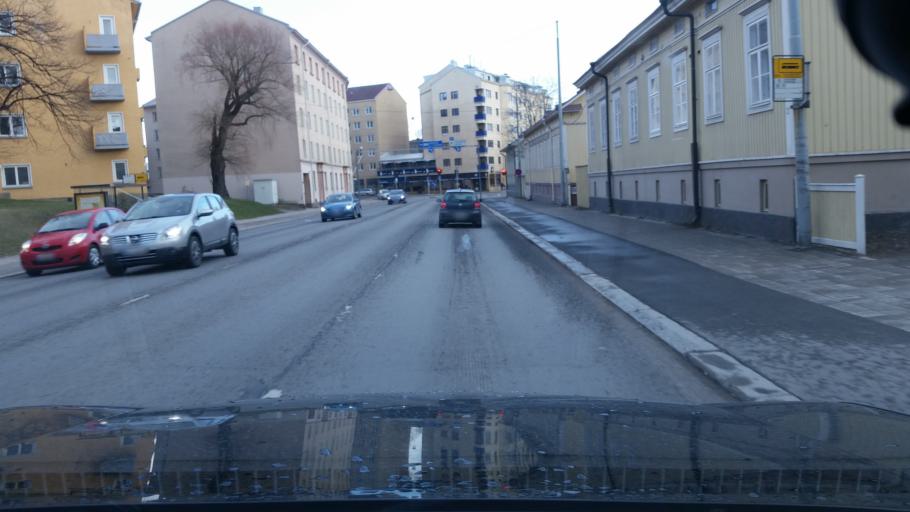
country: FI
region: Varsinais-Suomi
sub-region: Turku
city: Turku
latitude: 60.4401
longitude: 22.2577
